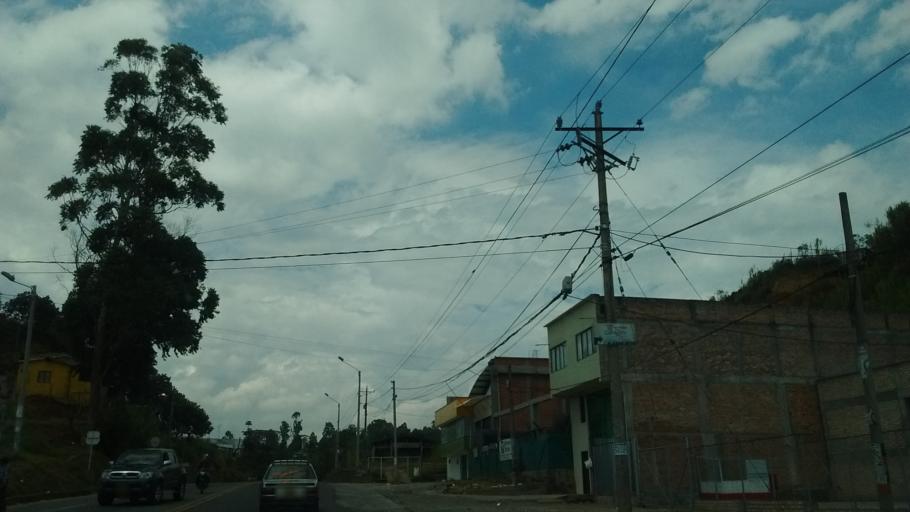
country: CO
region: Cauca
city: Popayan
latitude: 2.4276
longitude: -76.6215
